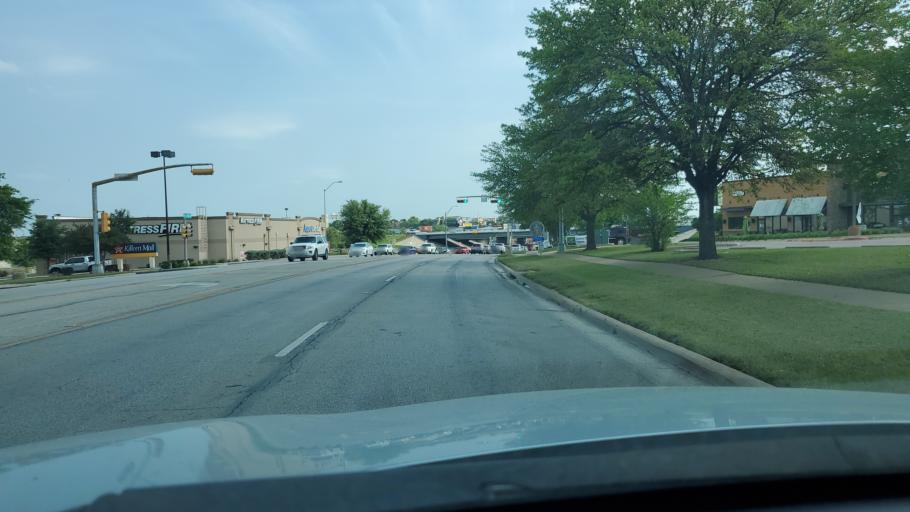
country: US
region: Texas
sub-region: Bell County
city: Killeen
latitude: 31.0933
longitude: -97.7205
